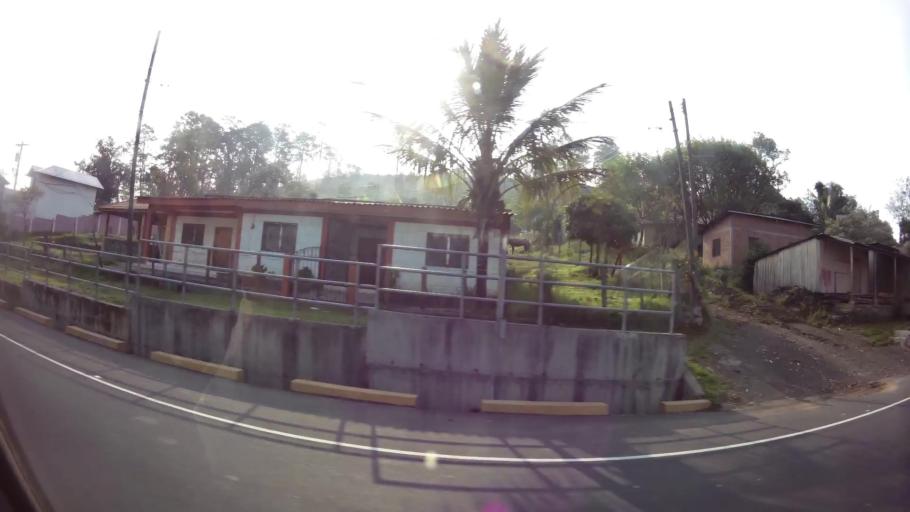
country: HN
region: Francisco Morazan
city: Zambrano
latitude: 14.2756
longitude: -87.4055
